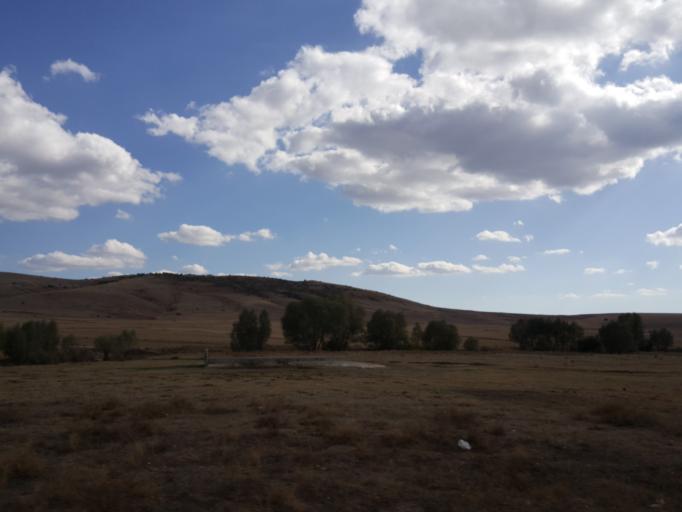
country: TR
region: Tokat
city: Sulusaray
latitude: 39.9863
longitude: 35.9522
